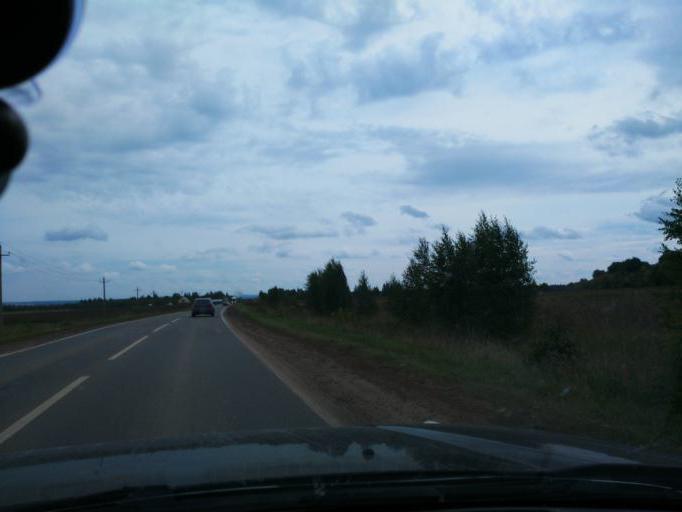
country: RU
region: Perm
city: Chernushka
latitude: 56.5091
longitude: 55.9724
